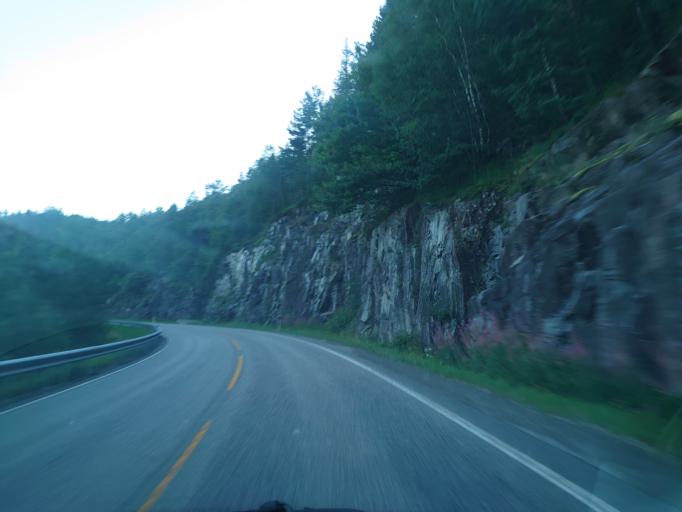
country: NO
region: Hordaland
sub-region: Osteroy
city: Lonevag
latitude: 60.6421
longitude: 5.4930
